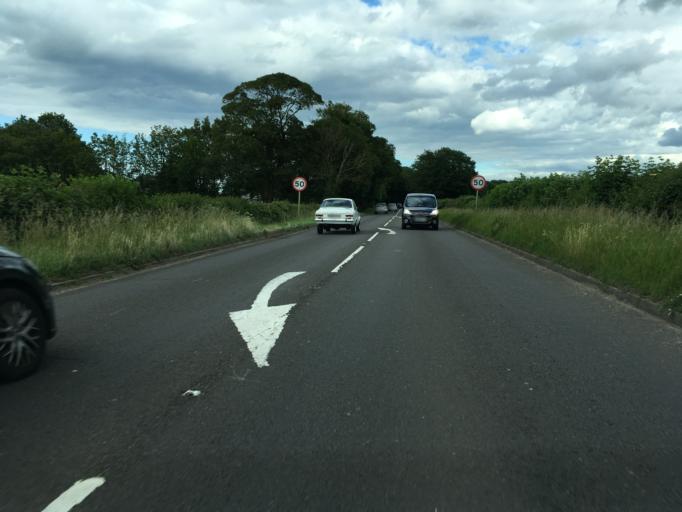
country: GB
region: England
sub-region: Buckinghamshire
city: Haddenham
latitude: 51.7822
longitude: -0.9366
